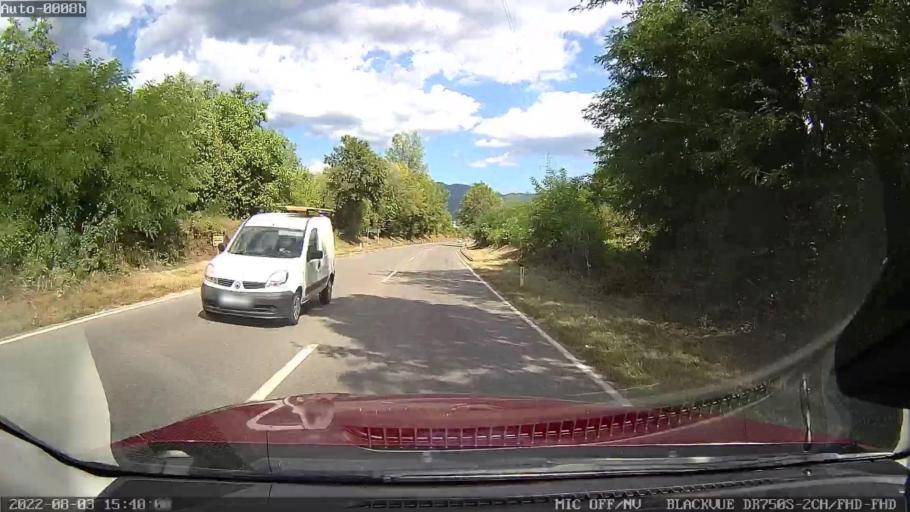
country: SI
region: Nova Gorica
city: Kromberk
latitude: 45.9572
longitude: 13.6644
